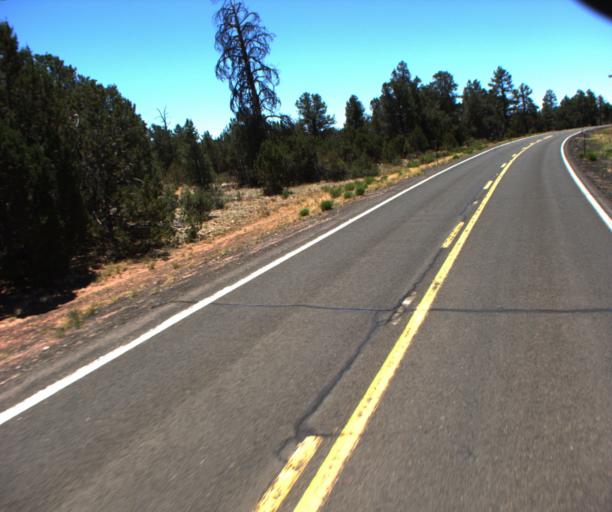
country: US
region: Arizona
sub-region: Gila County
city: Star Valley
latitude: 34.6960
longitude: -111.1069
